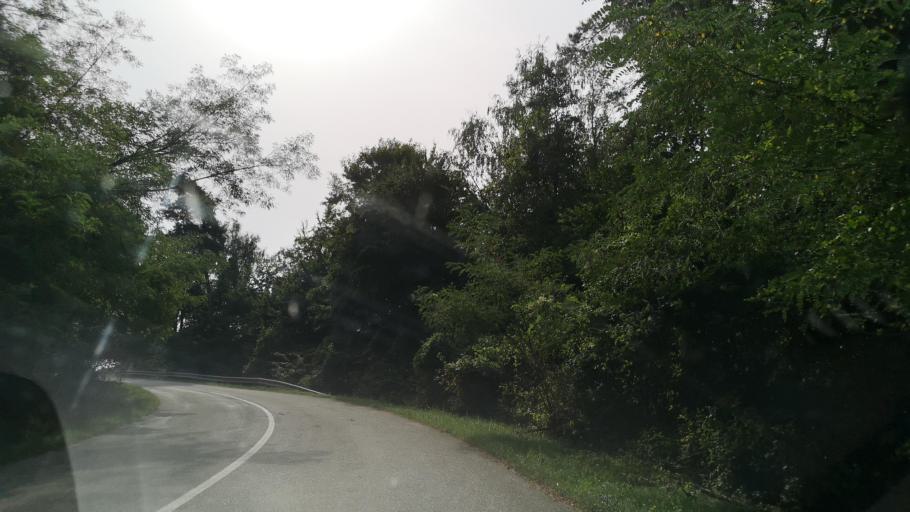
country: SK
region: Banskobystricky
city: Revuca
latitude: 48.5769
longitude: 20.0386
